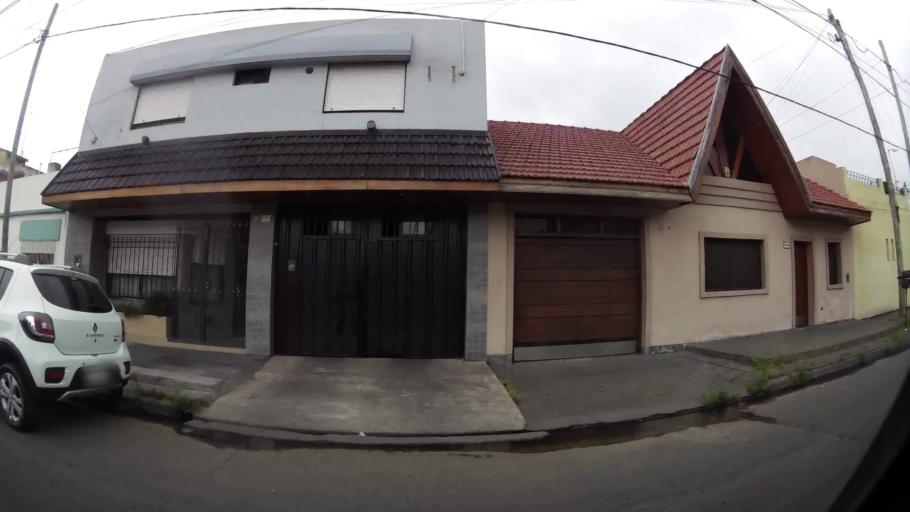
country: AR
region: Buenos Aires
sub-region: Partido de Avellaneda
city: Avellaneda
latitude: -34.6731
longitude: -58.3477
